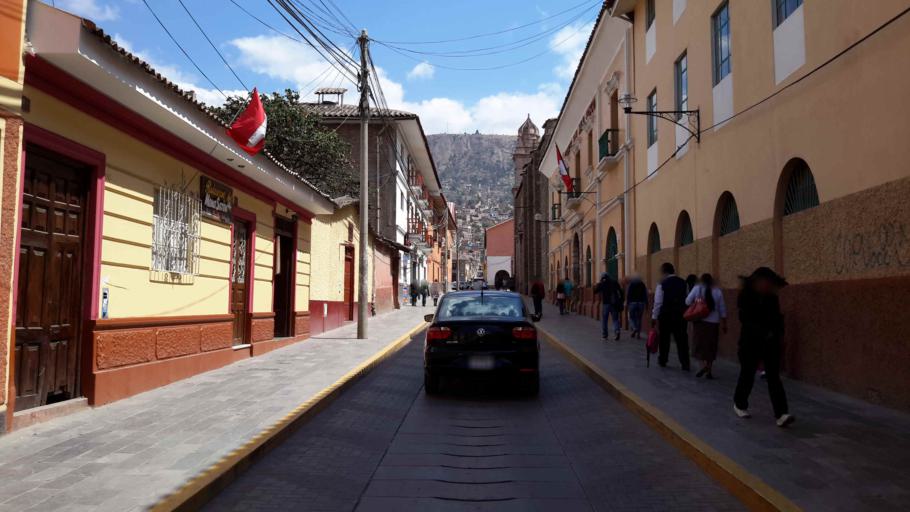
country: PE
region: Ayacucho
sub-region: Provincia de Huamanga
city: Ayacucho
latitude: -13.1602
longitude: -74.2240
